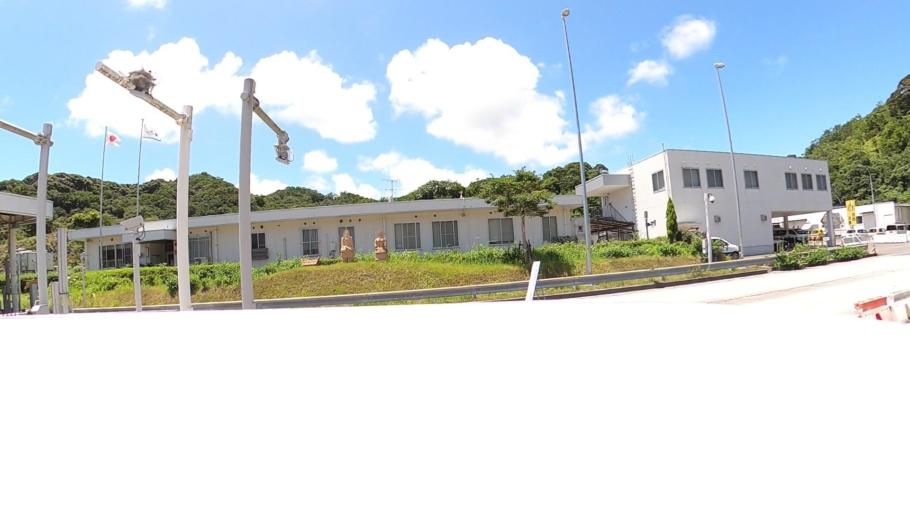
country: JP
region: Miyazaki
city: Nobeoka
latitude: 32.5031
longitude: 131.6620
